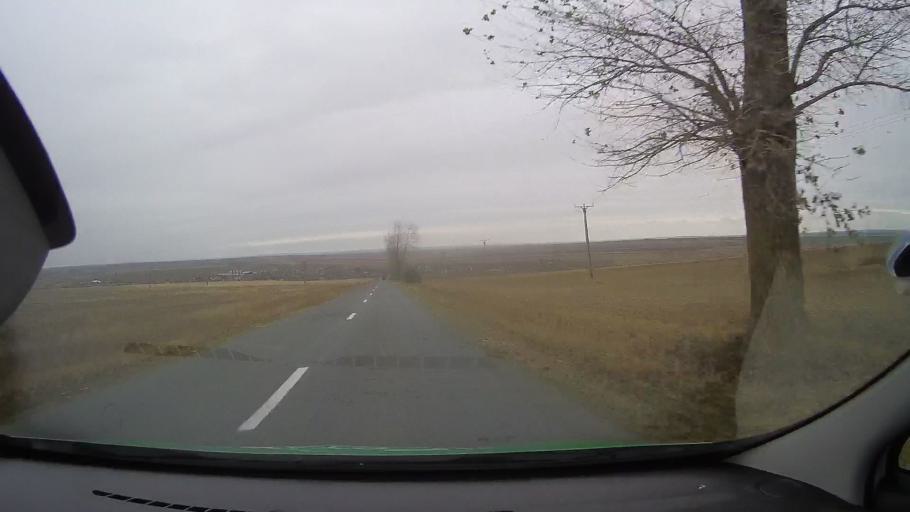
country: RO
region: Constanta
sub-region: Comuna Pantelimon
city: Pantelimon
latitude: 44.5911
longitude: 28.3199
